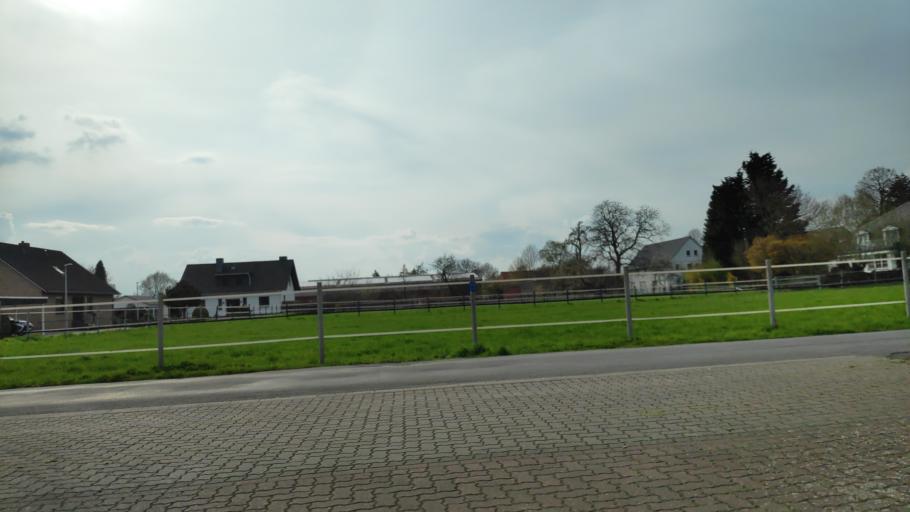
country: DE
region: North Rhine-Westphalia
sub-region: Regierungsbezirk Detmold
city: Minden
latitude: 52.2888
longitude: 8.8731
